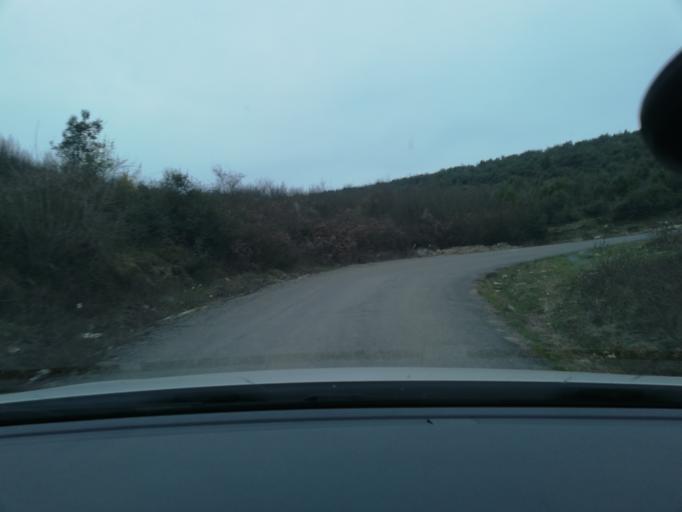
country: TR
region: Zonguldak
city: Saltukova
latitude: 41.5179
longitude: 32.0798
